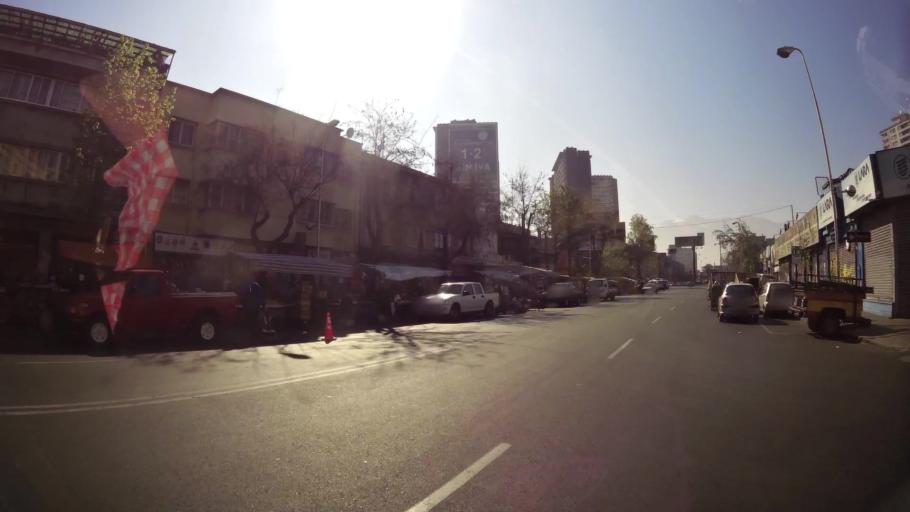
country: CL
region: Santiago Metropolitan
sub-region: Provincia de Santiago
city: Santiago
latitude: -33.4517
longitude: -70.6324
